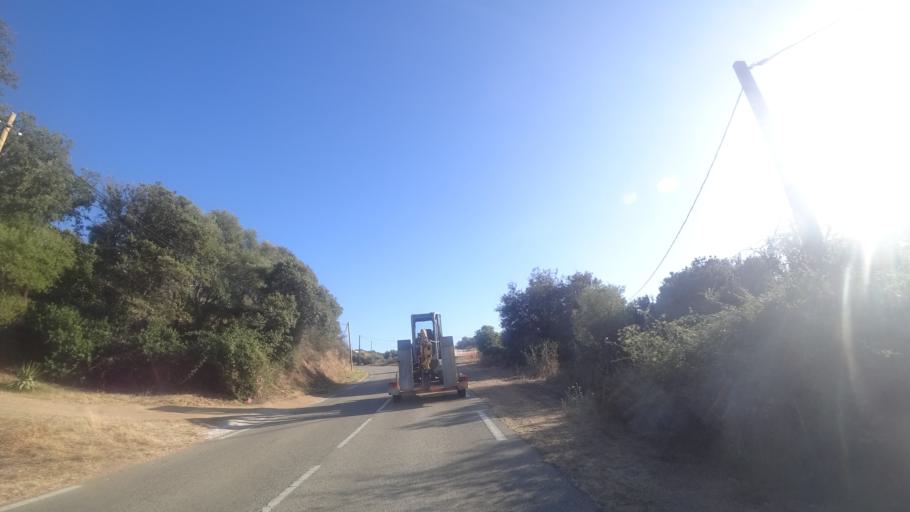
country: FR
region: Corsica
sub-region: Departement de la Corse-du-Sud
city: Cargese
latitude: 42.1478
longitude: 8.6035
